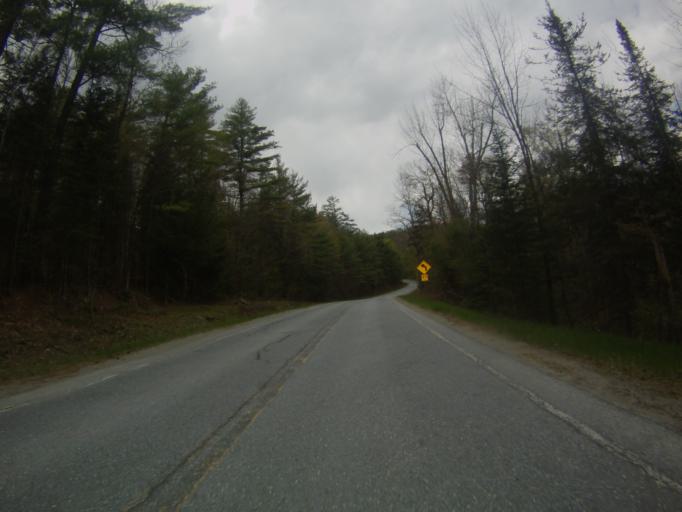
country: US
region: New York
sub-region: Essex County
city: Mineville
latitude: 44.0946
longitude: -73.5525
